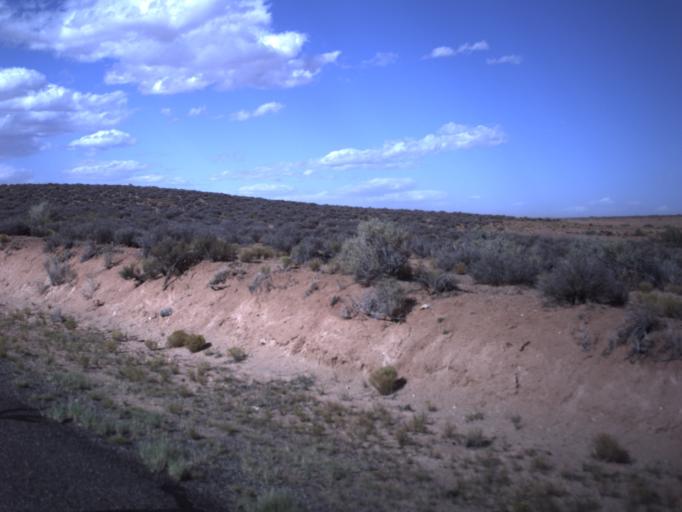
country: US
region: Utah
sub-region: Wayne County
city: Loa
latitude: 38.0920
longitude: -110.6187
